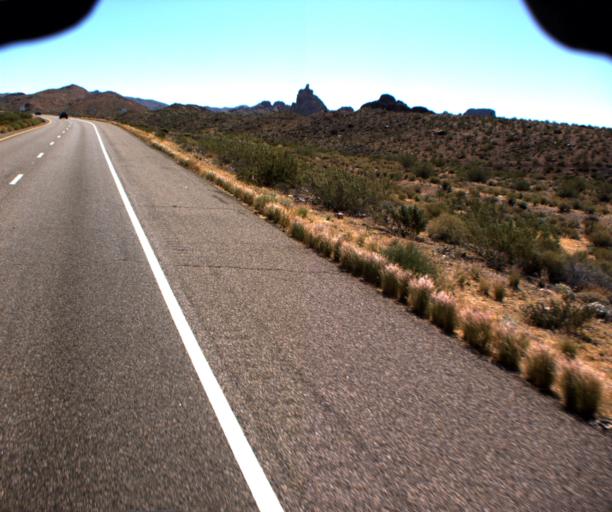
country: US
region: Nevada
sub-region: Clark County
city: Laughlin
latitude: 35.1854
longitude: -114.4575
